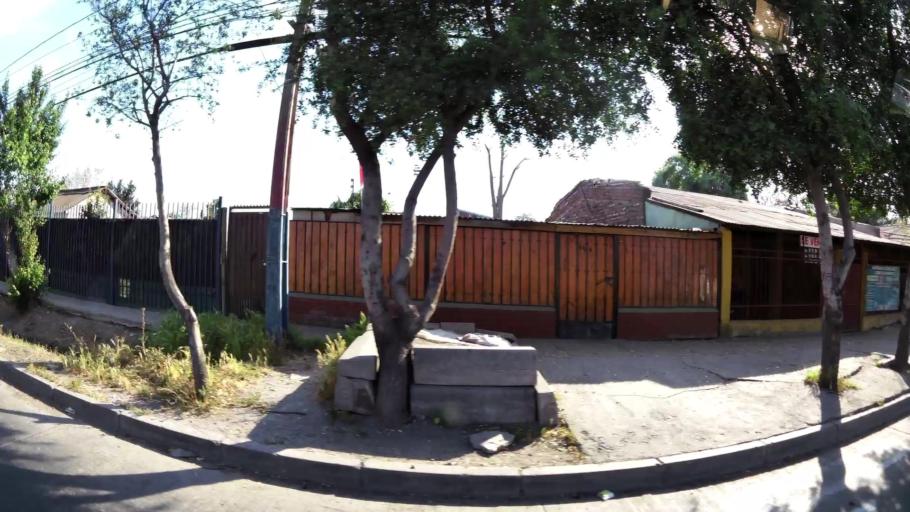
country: CL
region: Santiago Metropolitan
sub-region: Provincia de Maipo
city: San Bernardo
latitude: -33.6068
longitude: -70.7078
